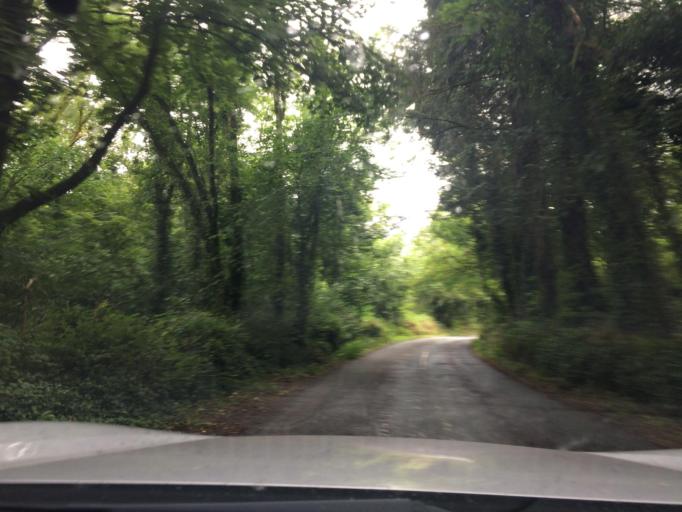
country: IE
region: Munster
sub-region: South Tipperary
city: Cluain Meala
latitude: 52.2090
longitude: -7.7325
